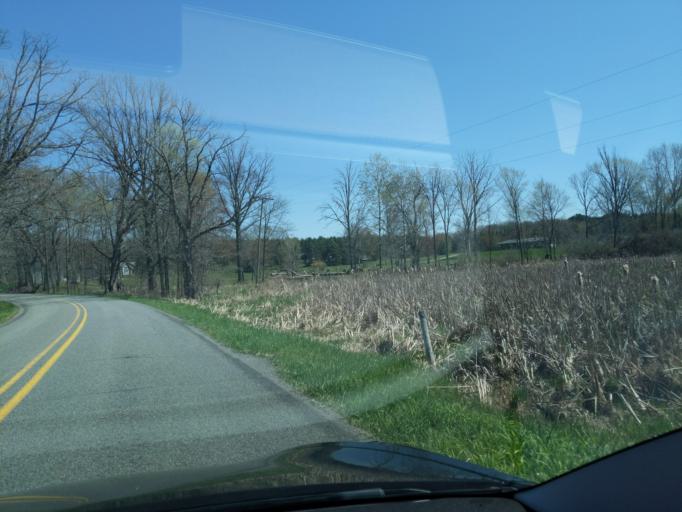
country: US
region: Michigan
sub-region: Ingham County
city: Stockbridge
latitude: 42.4870
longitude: -84.1809
